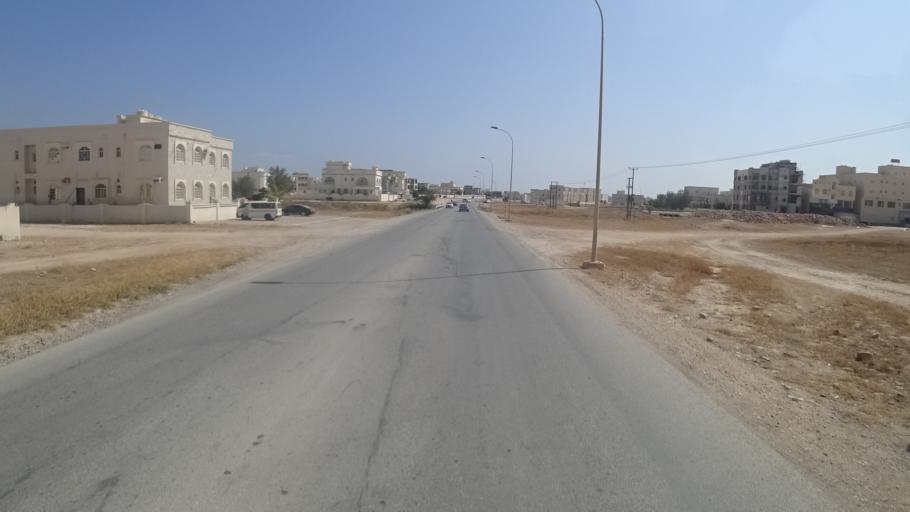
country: OM
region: Zufar
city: Salalah
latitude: 17.0121
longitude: 54.0243
